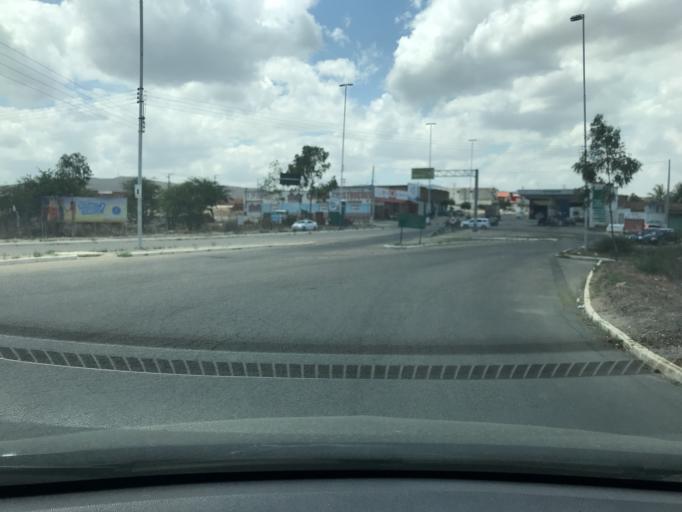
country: BR
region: Pernambuco
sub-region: Bezerros
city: Bezerros
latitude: -8.2467
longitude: -35.7590
